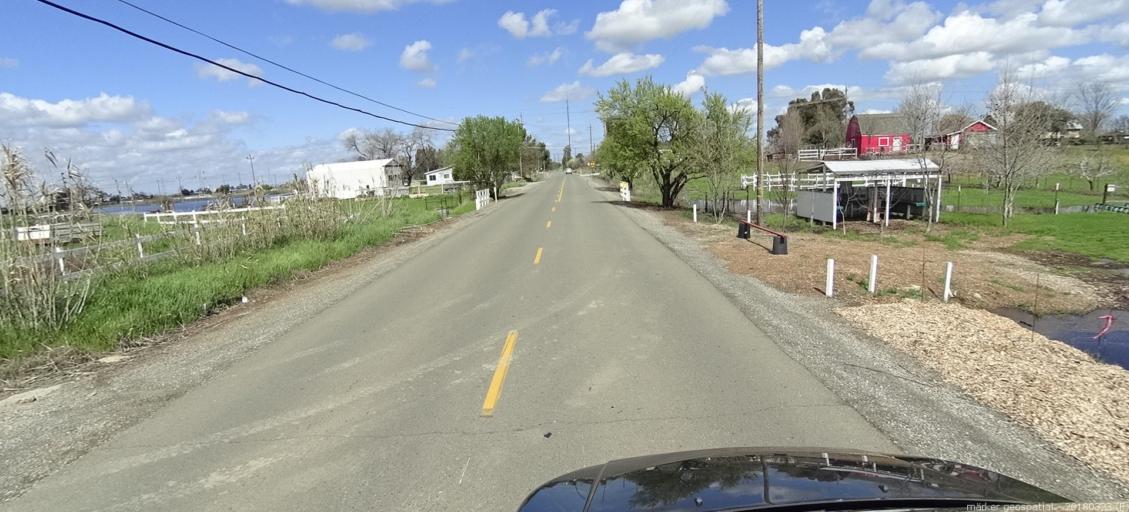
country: US
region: California
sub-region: Sacramento County
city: Elverta
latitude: 38.6972
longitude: -121.4746
